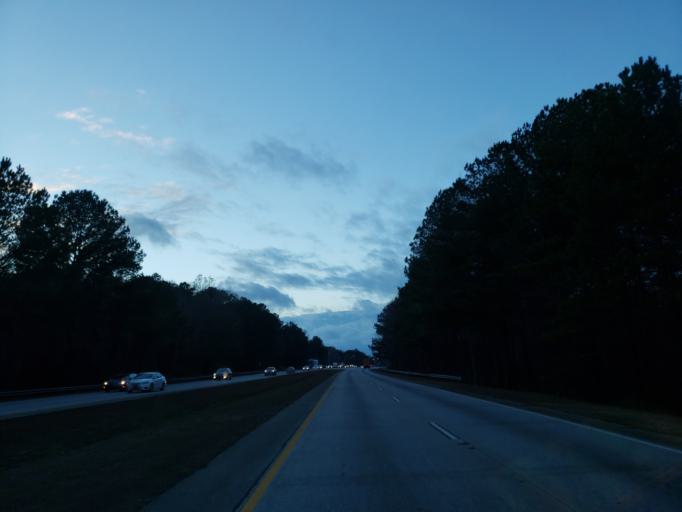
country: US
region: Georgia
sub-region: Fulton County
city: Union City
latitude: 33.6833
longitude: -84.5617
